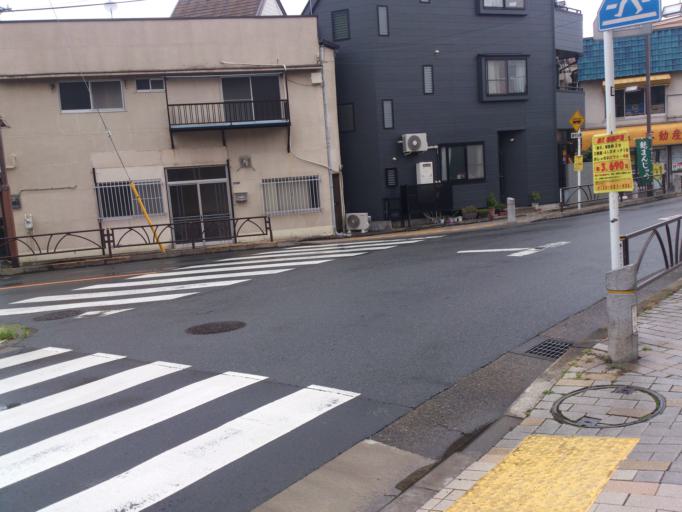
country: JP
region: Chiba
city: Matsudo
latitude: 35.7525
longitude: 139.8710
